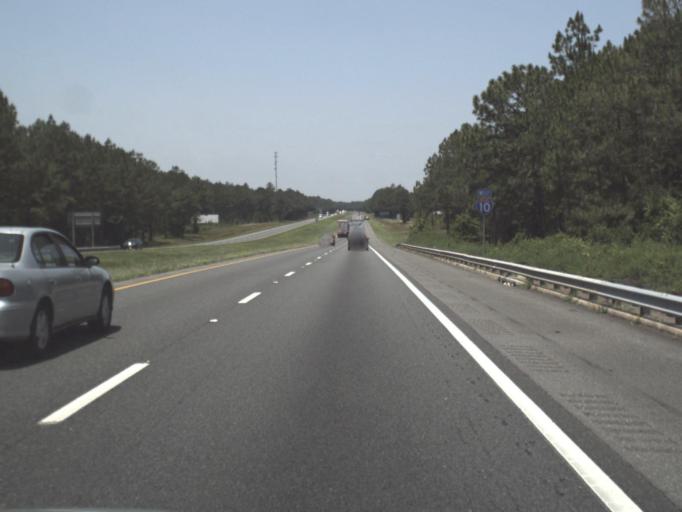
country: US
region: Florida
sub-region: Baker County
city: Macclenny
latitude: 30.2408
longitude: -82.3068
